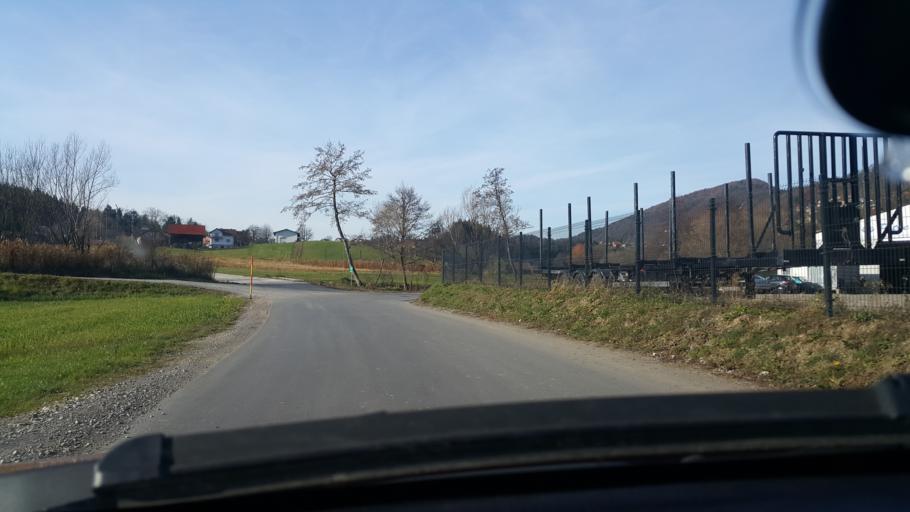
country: SI
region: Velenje
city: Velenje
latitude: 46.3444
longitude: 15.1659
